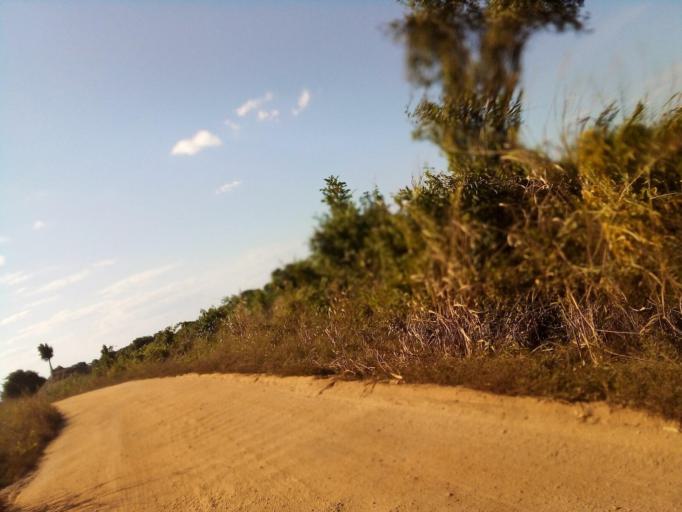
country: MZ
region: Zambezia
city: Quelimane
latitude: -17.5596
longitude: 36.6358
